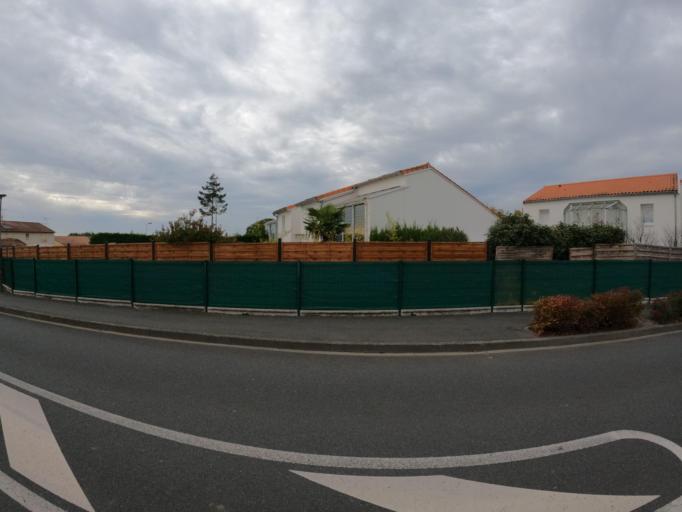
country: FR
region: Pays de la Loire
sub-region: Departement de Maine-et-Loire
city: Saint-Christophe-du-Bois
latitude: 47.0334
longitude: -0.9404
